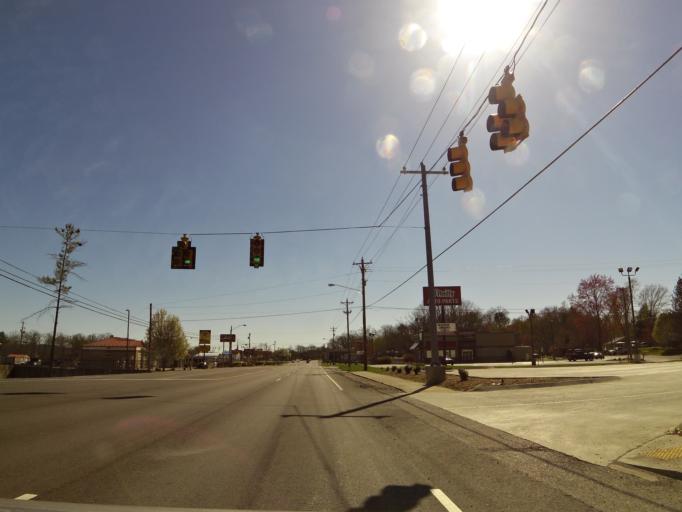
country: US
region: Tennessee
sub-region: Scott County
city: Oneida
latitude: 36.5138
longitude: -84.5087
